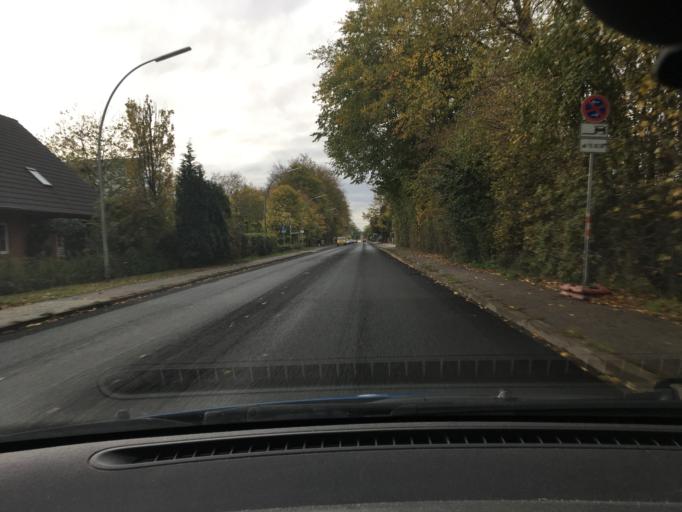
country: DE
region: Schleswig-Holstein
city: Wentorf bei Hamburg
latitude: 53.4912
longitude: 10.2648
